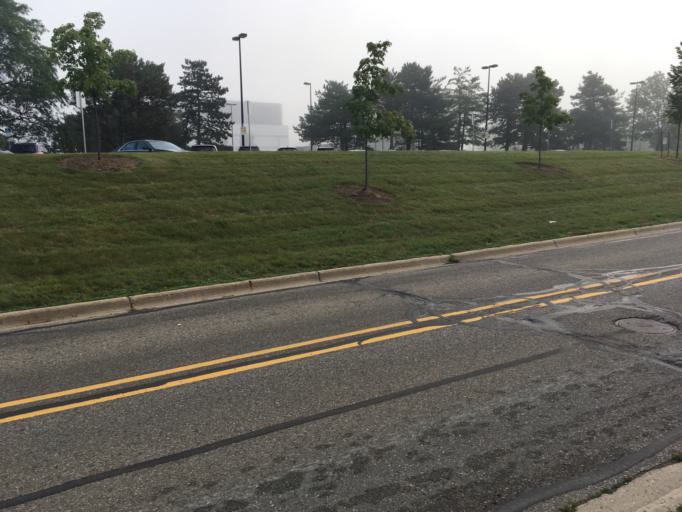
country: US
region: Michigan
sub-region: Washtenaw County
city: Ann Arbor
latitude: 42.2971
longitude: -83.7030
